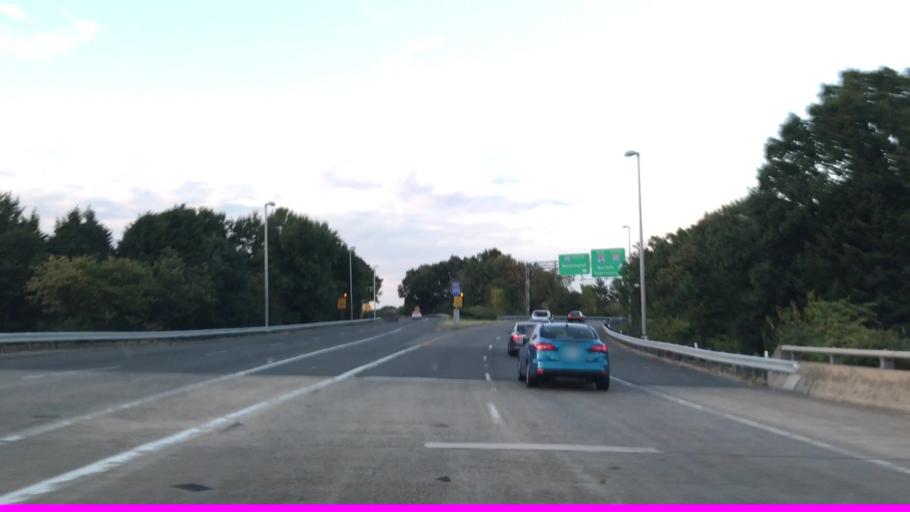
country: US
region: Virginia
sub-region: Henrico County
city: Lakeside
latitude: 37.5840
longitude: -77.4742
